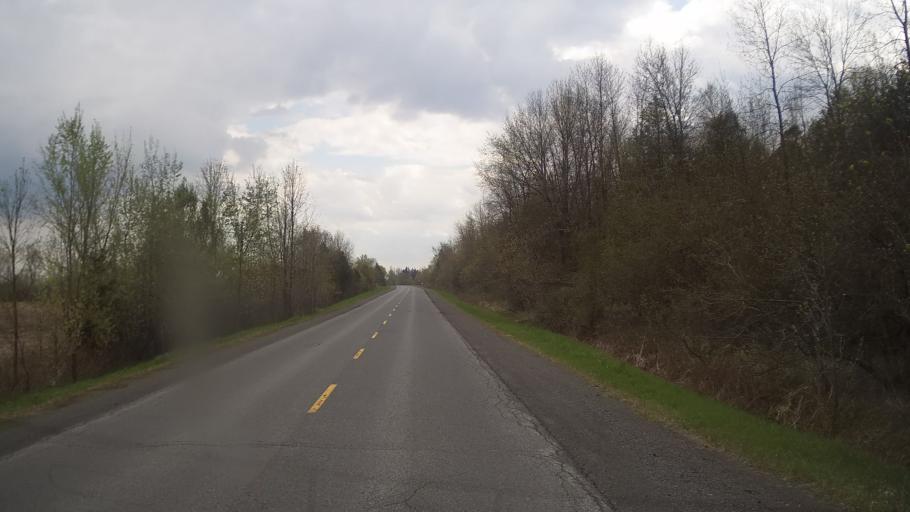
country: CA
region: Ontario
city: Hawkesbury
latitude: 45.5251
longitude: -74.5624
